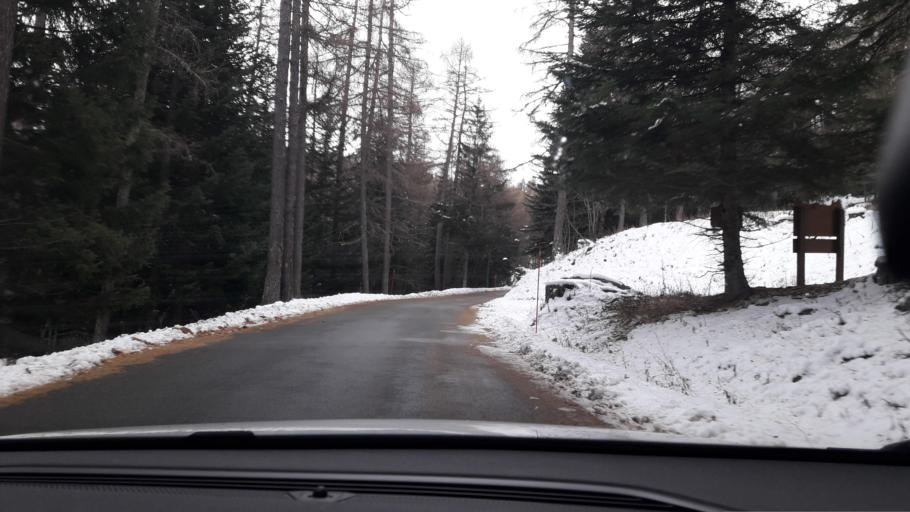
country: FR
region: Rhone-Alpes
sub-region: Departement de la Savoie
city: Saint-Michel-de-Maurienne
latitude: 45.2216
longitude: 6.4167
